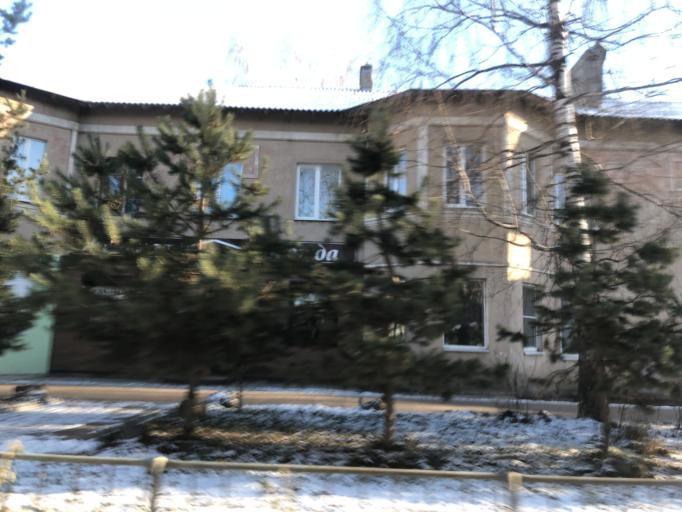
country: RU
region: Tverskaya
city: Rzhev
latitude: 56.2607
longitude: 34.3505
